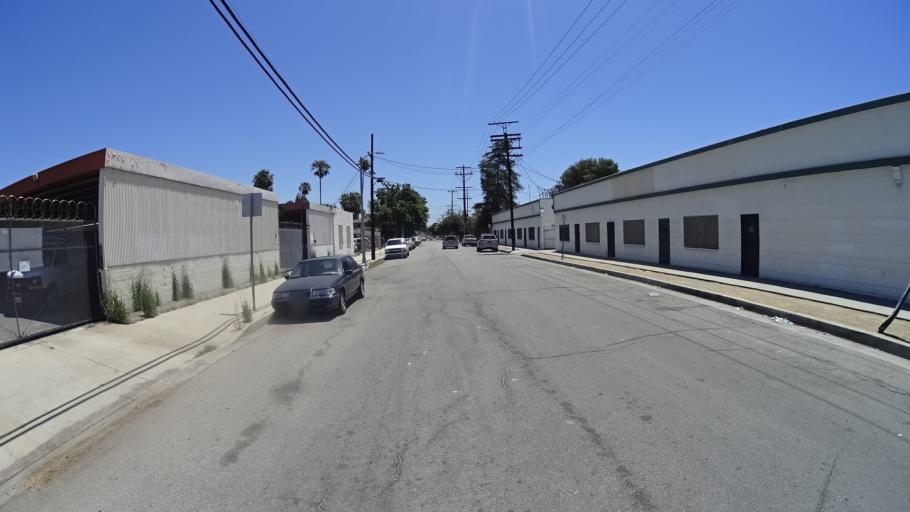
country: US
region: California
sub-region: Los Angeles County
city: Northridge
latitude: 34.1994
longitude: -118.5333
